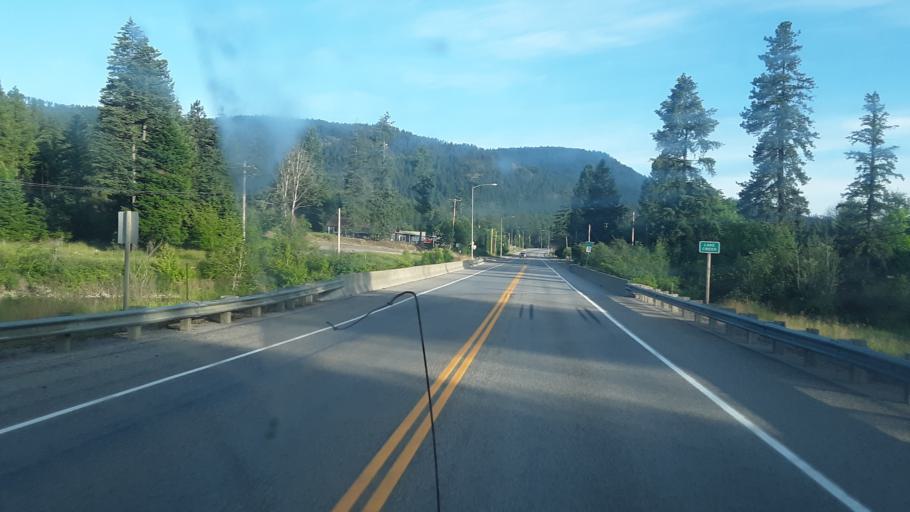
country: US
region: Montana
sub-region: Lincoln County
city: Libby
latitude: 48.4489
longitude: -115.8783
